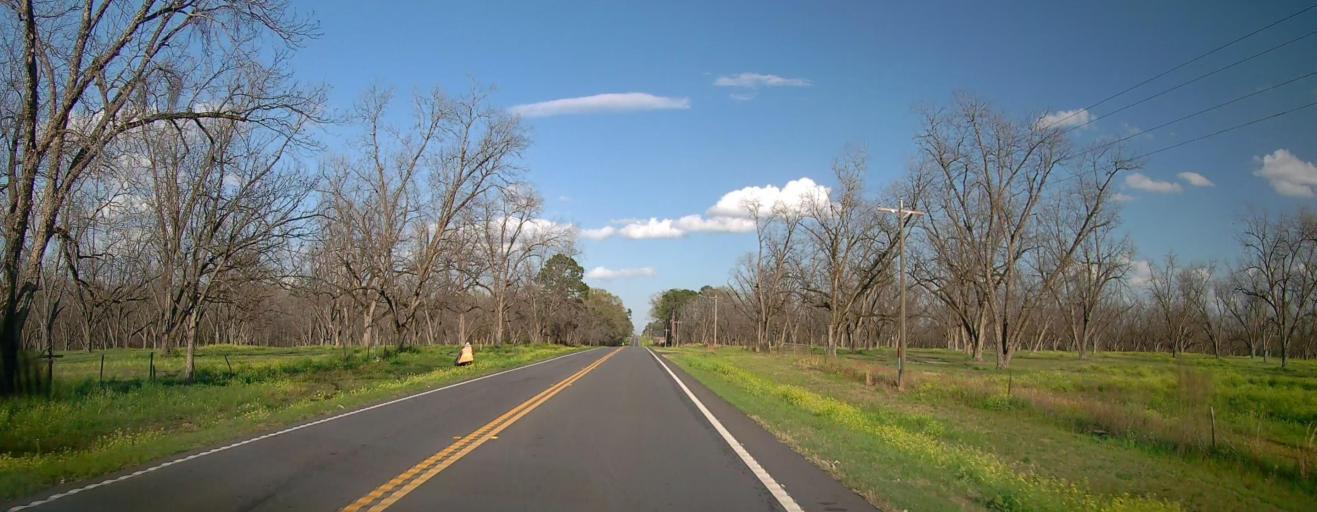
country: US
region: Georgia
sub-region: Toombs County
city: Vidalia
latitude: 32.1978
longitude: -82.5018
